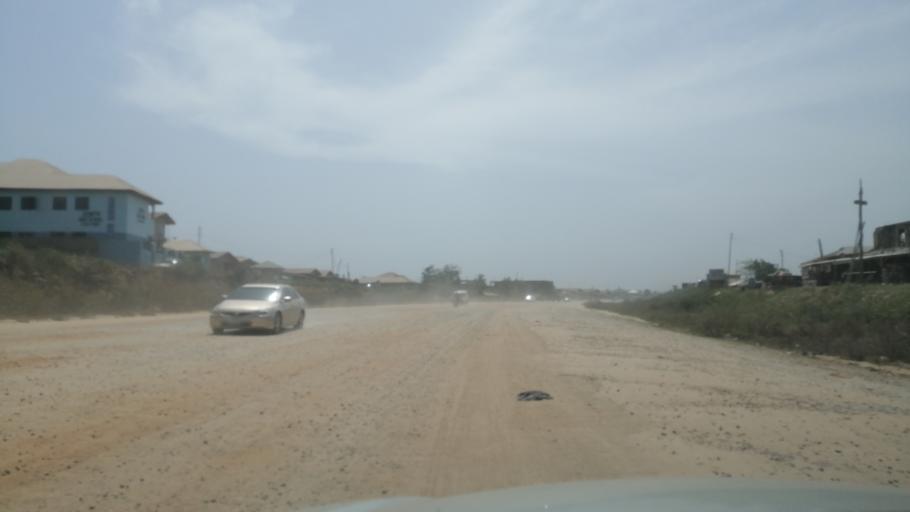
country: NG
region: Osun
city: Osogbo
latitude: 7.7850
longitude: 4.5799
